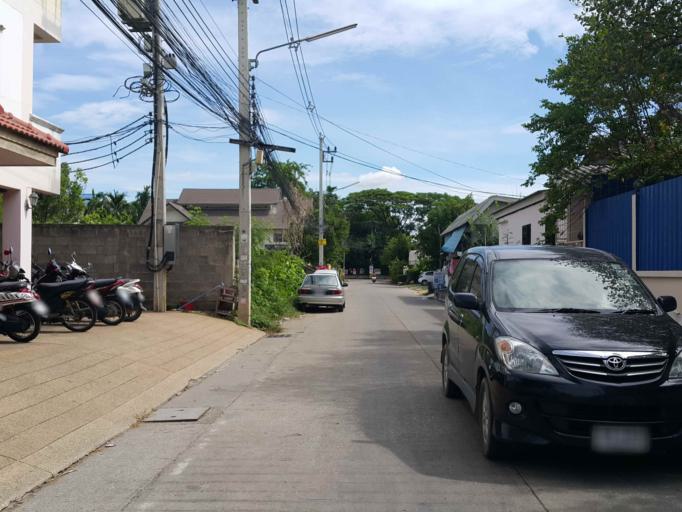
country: TH
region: Chiang Mai
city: Chiang Mai
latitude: 18.7715
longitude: 98.9851
